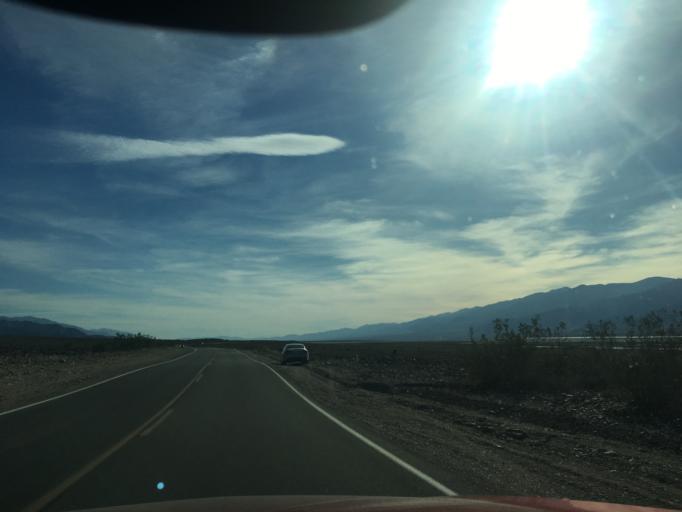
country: US
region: Nevada
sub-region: Nye County
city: Beatty
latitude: 36.5246
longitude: -116.8828
